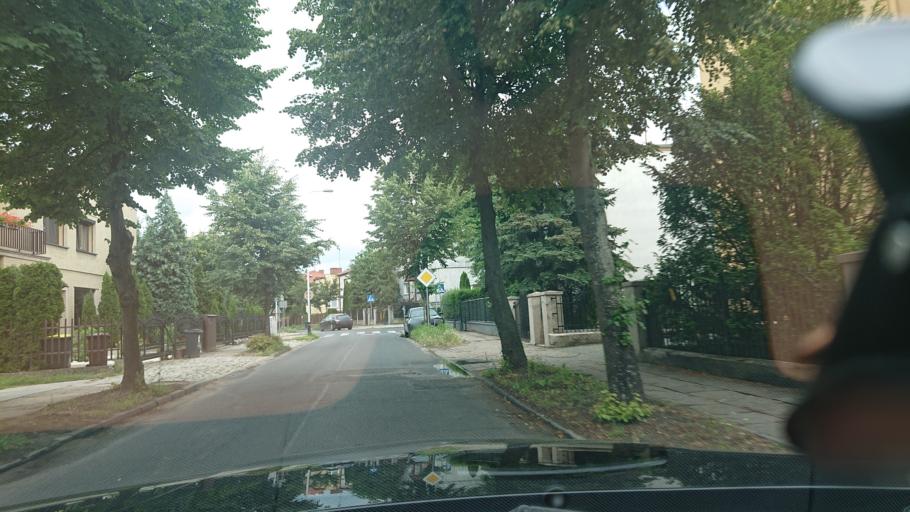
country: PL
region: Greater Poland Voivodeship
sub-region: Powiat gnieznienski
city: Gniezno
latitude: 52.5357
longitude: 17.6160
